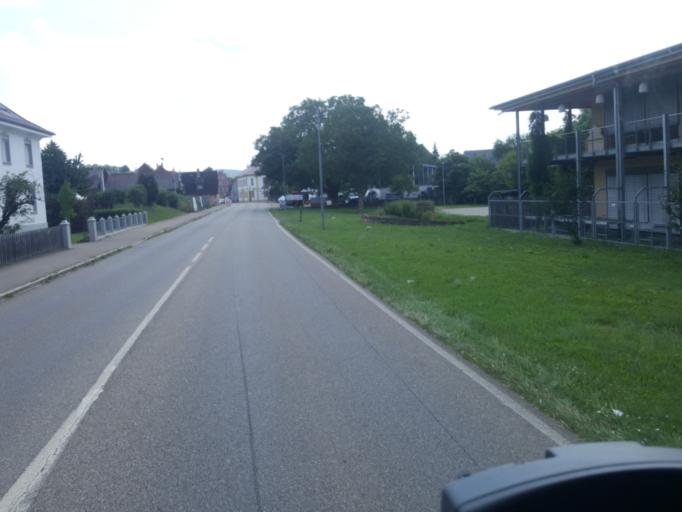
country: DE
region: Baden-Wuerttemberg
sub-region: Freiburg Region
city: Buggingen
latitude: 47.8321
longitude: 7.6213
